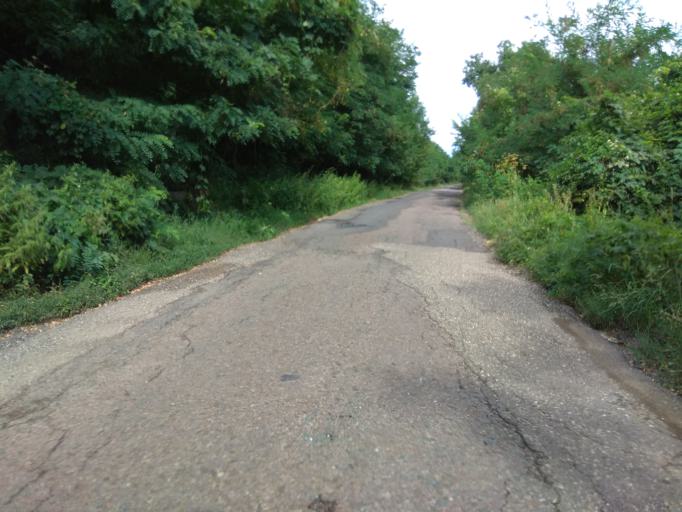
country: HU
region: Borsod-Abauj-Zemplen
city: Borsodnadasd
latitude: 48.0277
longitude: 20.2728
